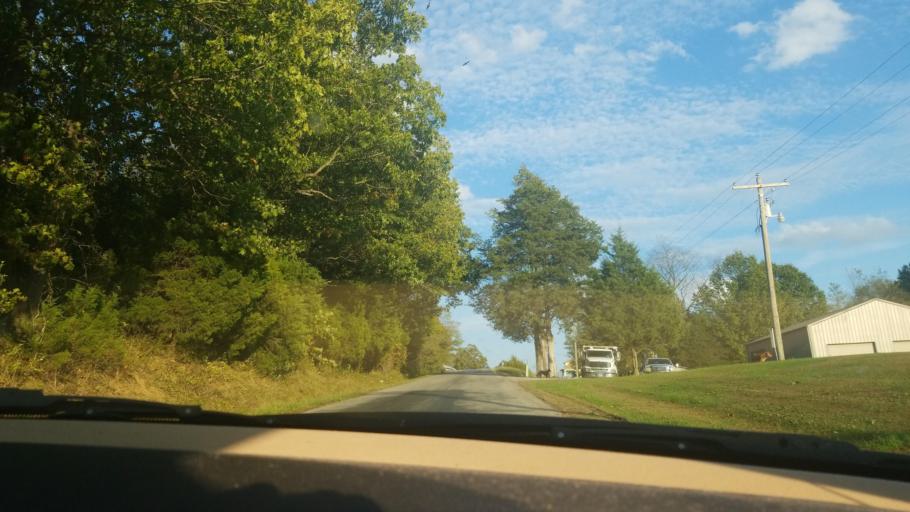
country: US
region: Illinois
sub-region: Saline County
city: Carrier Mills
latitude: 37.7721
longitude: -88.7161
